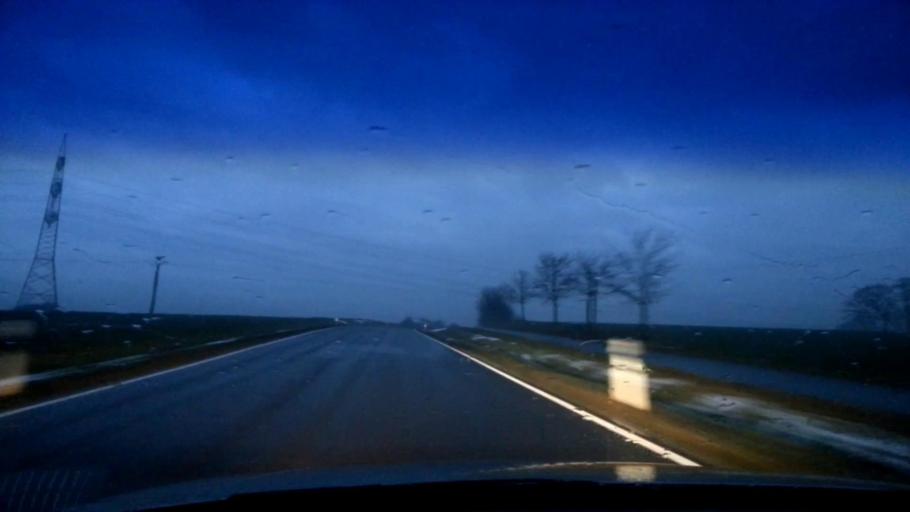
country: DE
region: Bavaria
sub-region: Upper Franconia
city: Memmelsdorf
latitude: 49.9500
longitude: 10.9554
